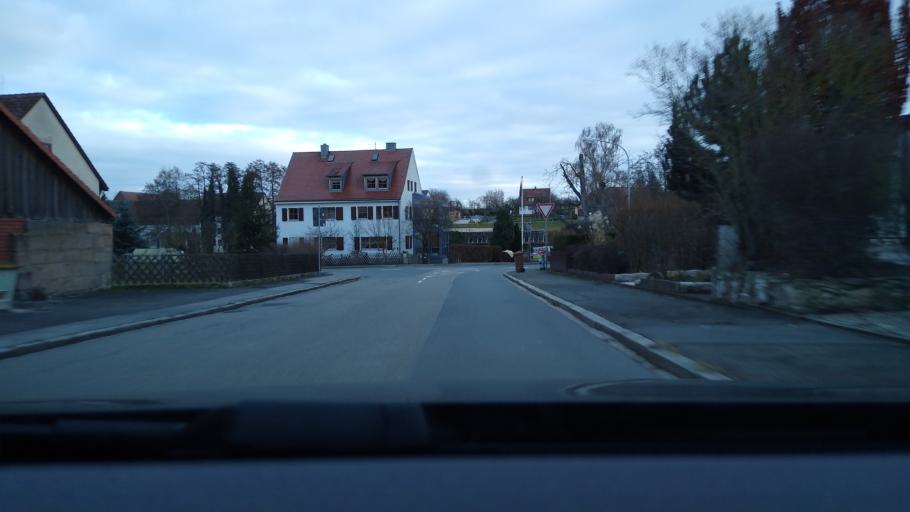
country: DE
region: Bavaria
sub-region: Regierungsbezirk Mittelfranken
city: Stein
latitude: 49.4040
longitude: 10.9896
